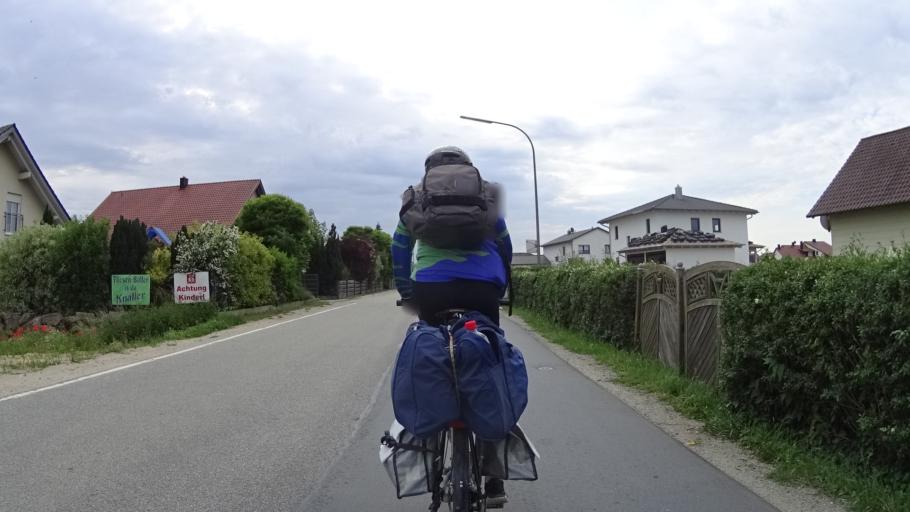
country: DE
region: Bavaria
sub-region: Lower Bavaria
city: Parkstetten
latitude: 48.9189
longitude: 12.5875
